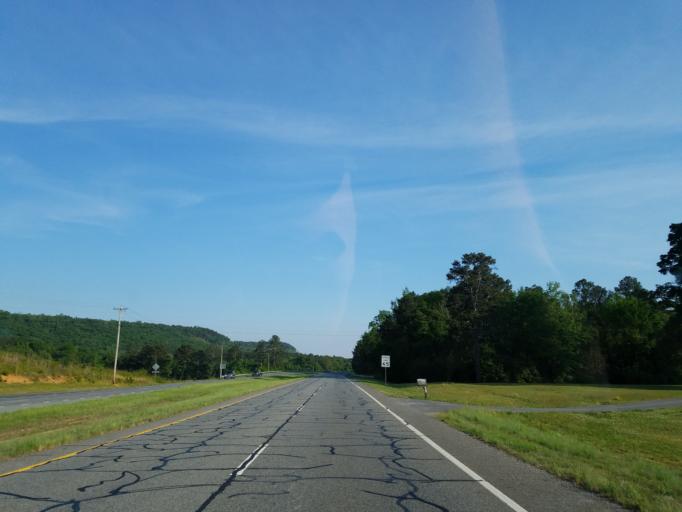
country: US
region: Georgia
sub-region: Chattooga County
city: Summerville
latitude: 34.4480
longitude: -85.2488
